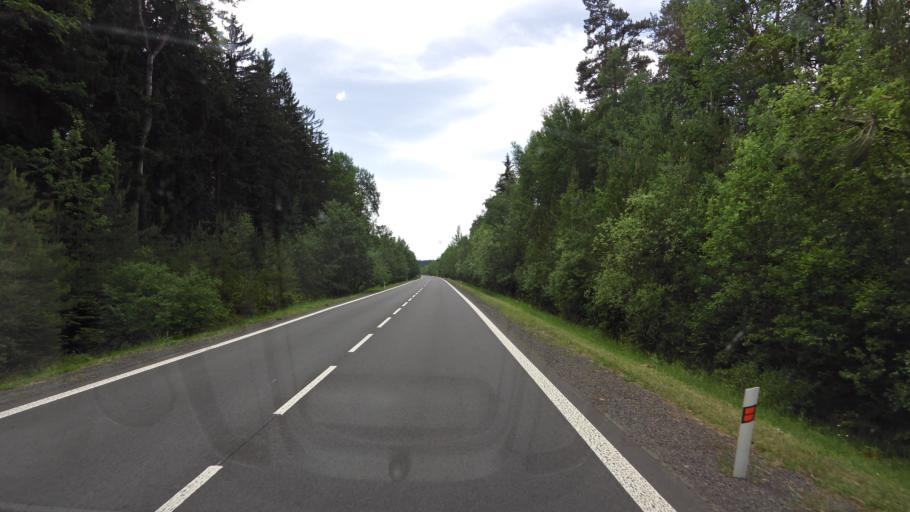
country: CZ
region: Plzensky
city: St'ahlavy
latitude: 49.7065
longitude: 13.5418
